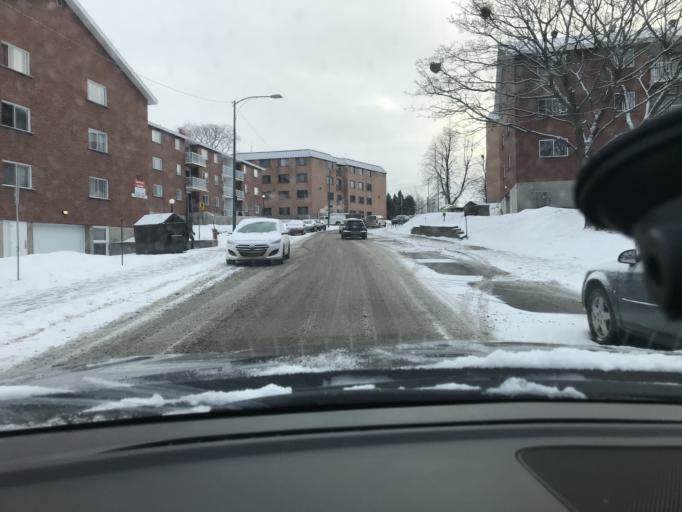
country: CA
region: Quebec
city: Quebec
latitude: 46.7887
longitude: -71.2760
